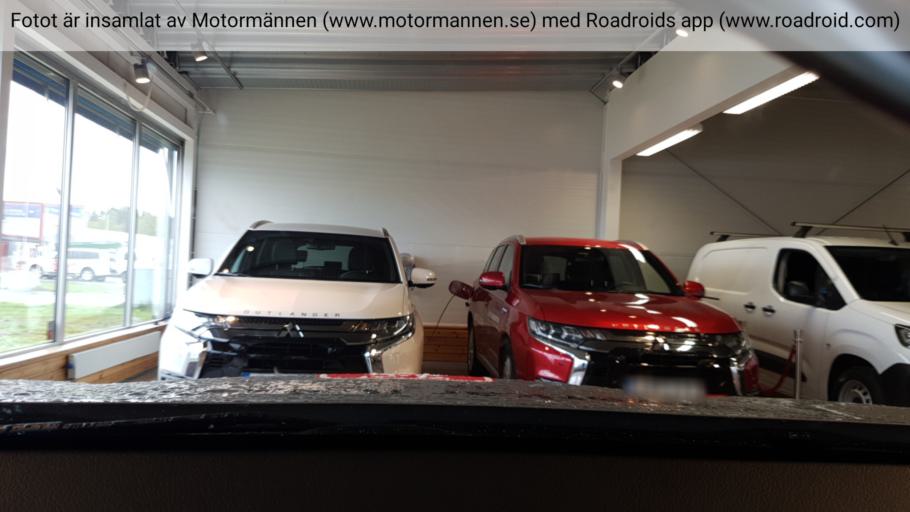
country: SE
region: Vaesterbotten
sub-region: Umea Kommun
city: Ersmark
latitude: 63.8506
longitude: 20.3114
